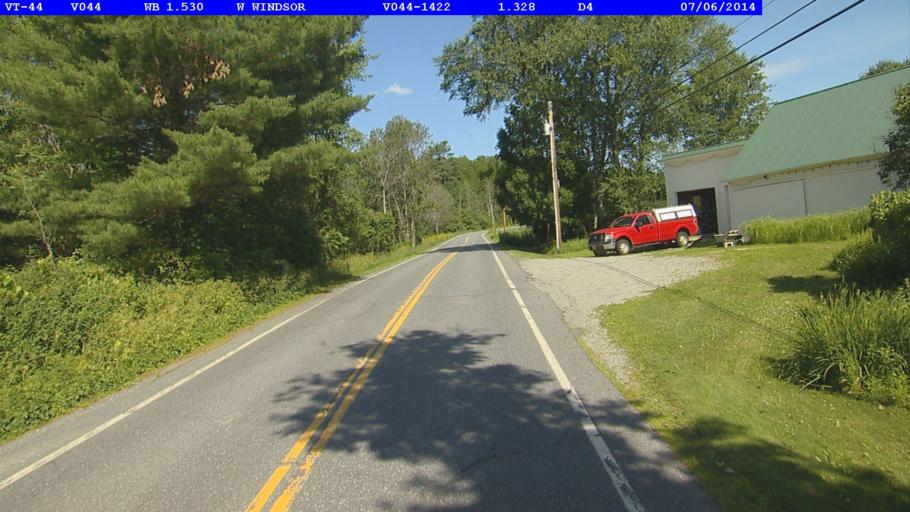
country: US
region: Vermont
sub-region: Windsor County
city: Windsor
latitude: 43.4558
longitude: -72.5159
